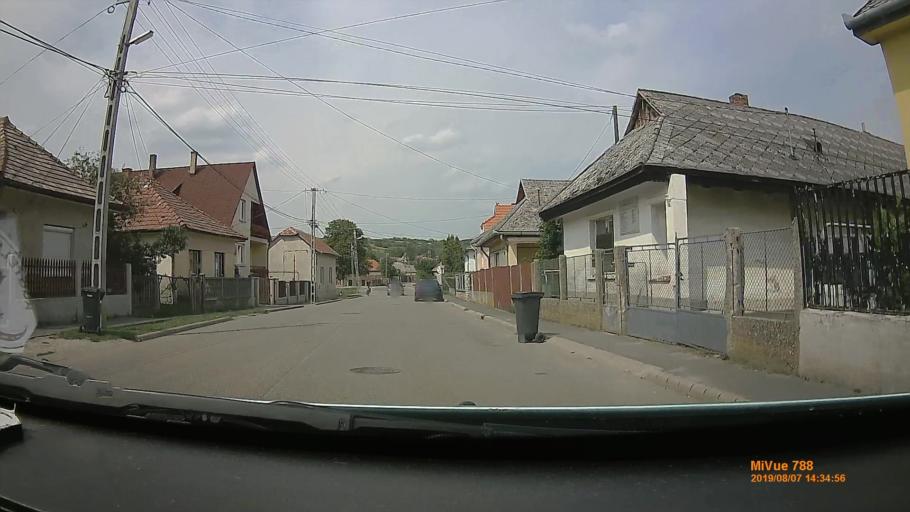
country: HU
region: Borsod-Abauj-Zemplen
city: Szikszo
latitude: 48.2036
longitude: 20.9264
